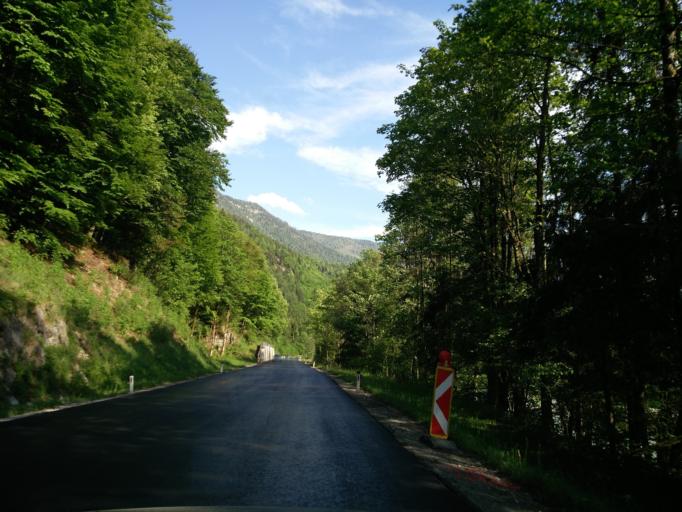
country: DE
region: Bavaria
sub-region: Upper Bavaria
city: Reit im Winkl
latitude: 47.6378
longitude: 12.4563
